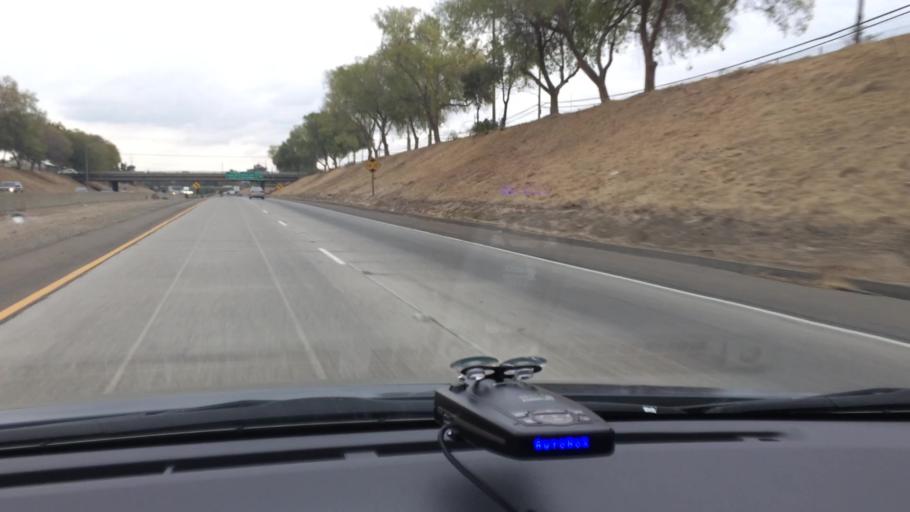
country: US
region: California
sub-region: San Joaquin County
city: Lodi
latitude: 38.1317
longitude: -121.2574
